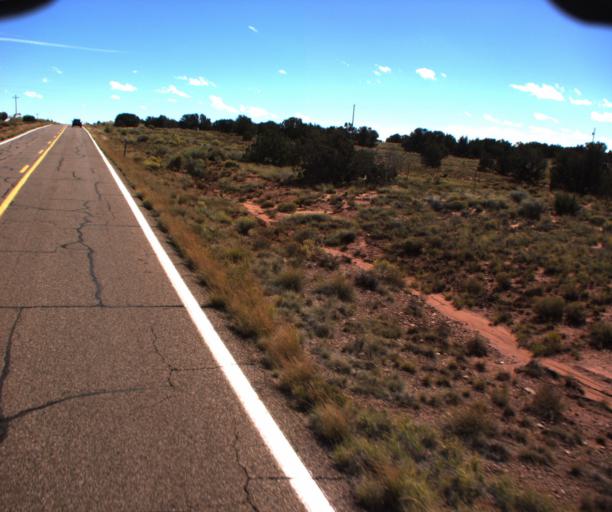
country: US
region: Arizona
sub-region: Apache County
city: Saint Johns
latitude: 34.5851
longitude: -109.6432
